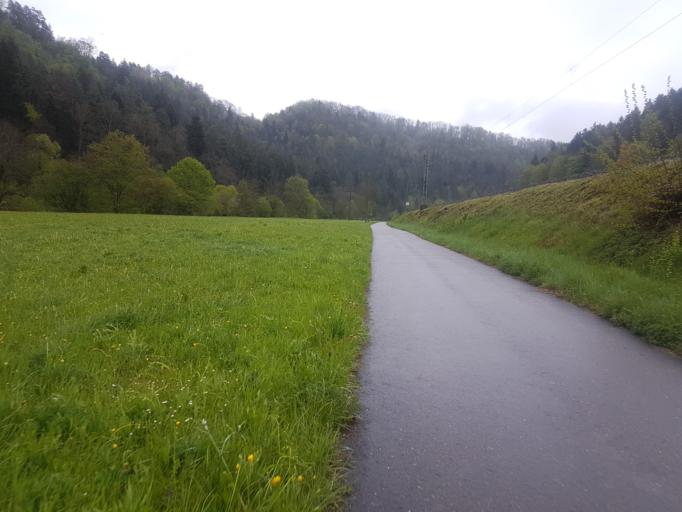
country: DE
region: Baden-Wuerttemberg
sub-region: Freiburg Region
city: Epfendorf
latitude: 48.2347
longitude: 8.6063
